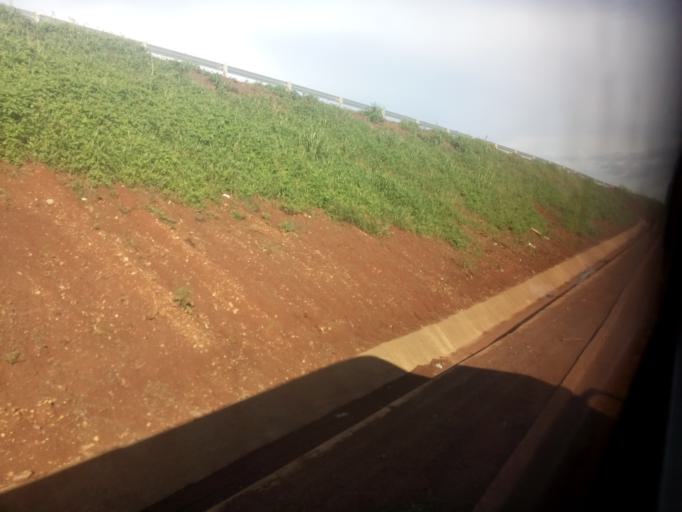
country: AR
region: Misiones
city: Garupa
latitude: -27.4531
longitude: -55.8649
